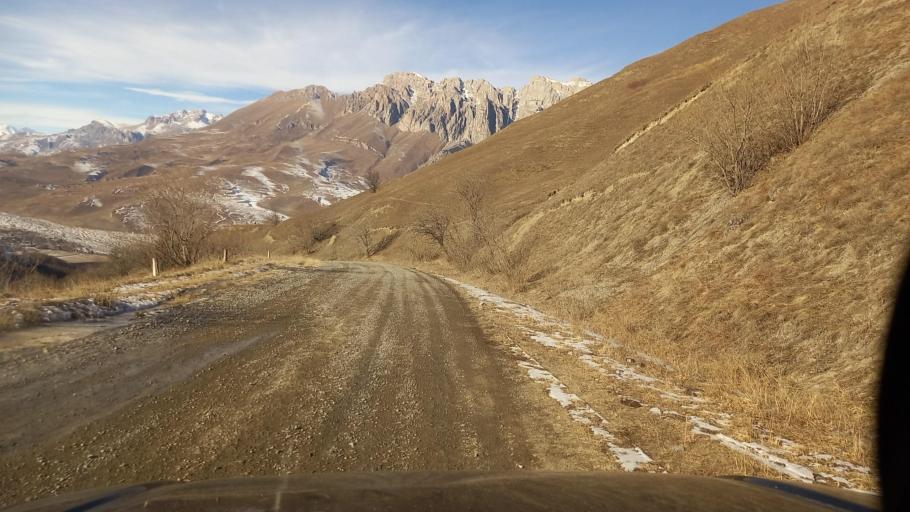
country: RU
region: North Ossetia
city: Verkhniy Fiagdon
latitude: 42.8364
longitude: 44.4740
